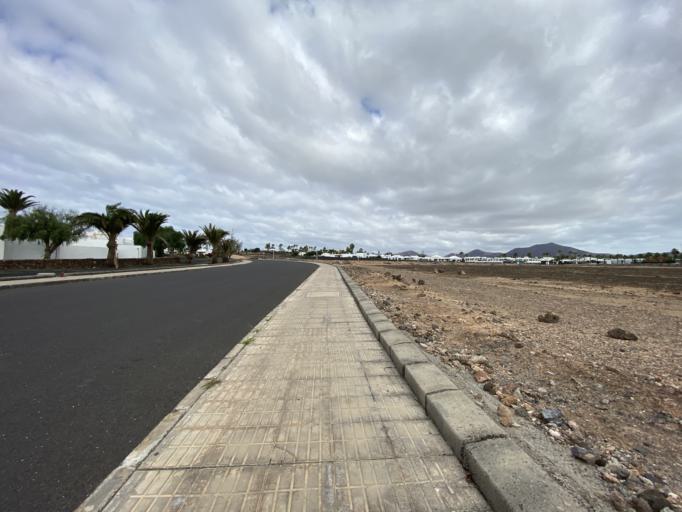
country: ES
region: Canary Islands
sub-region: Provincia de Las Palmas
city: Playa Blanca
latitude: 28.8627
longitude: -13.8463
